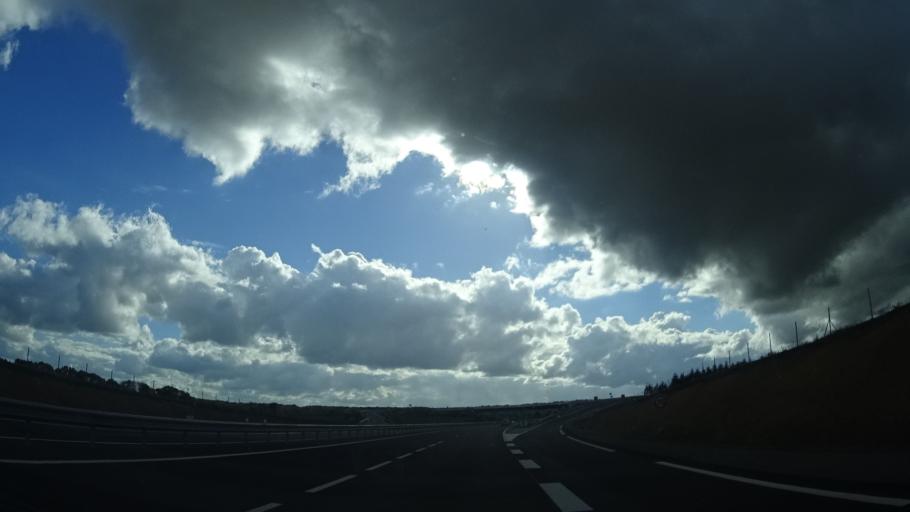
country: FR
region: Brittany
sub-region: Departement d'Ille-et-Vilaine
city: Pipriac
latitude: 47.7825
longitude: -1.9247
